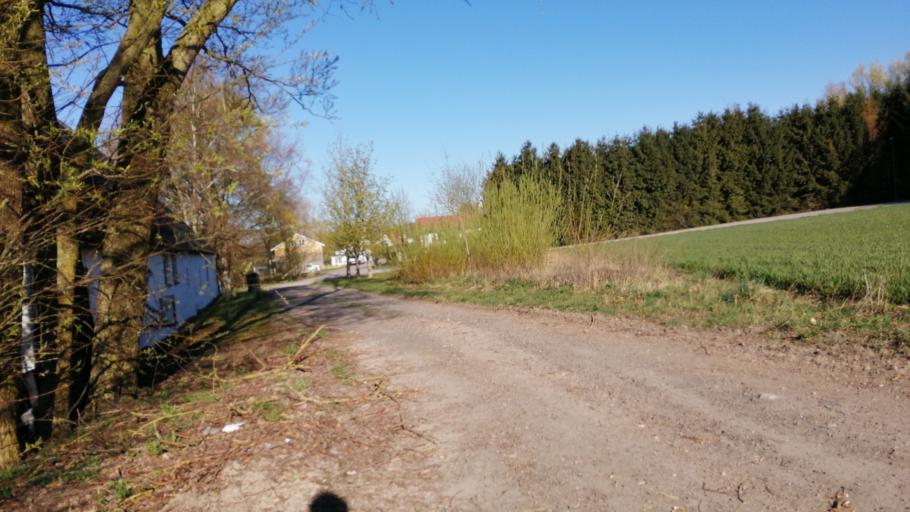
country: SE
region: Skane
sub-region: Landskrona
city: Asmundtorp
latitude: 55.8788
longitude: 13.0059
